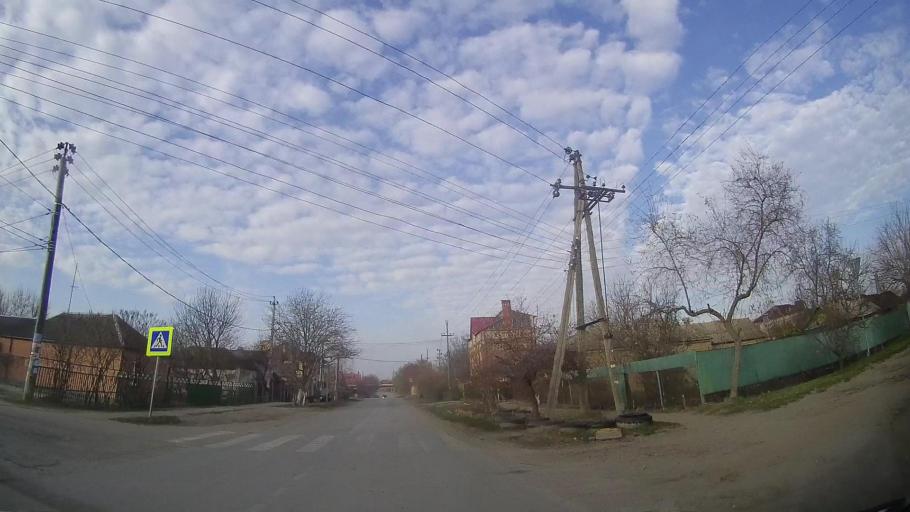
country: RU
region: Rostov
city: Bataysk
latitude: 47.1306
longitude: 39.7776
